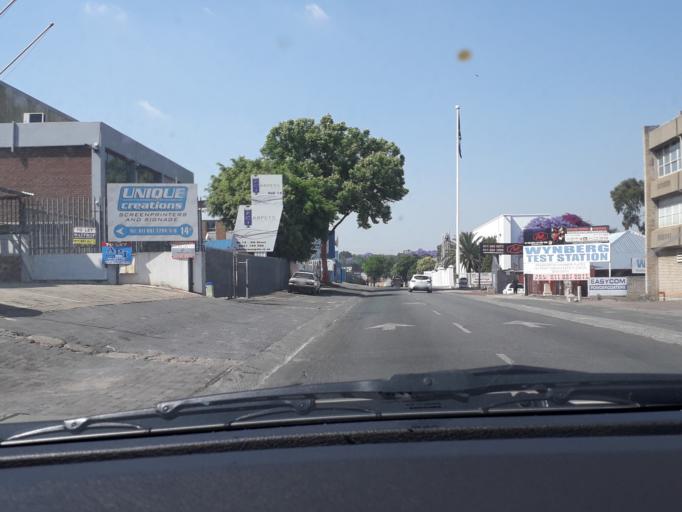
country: ZA
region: Gauteng
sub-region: City of Johannesburg Metropolitan Municipality
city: Modderfontein
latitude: -26.1125
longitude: 28.0811
